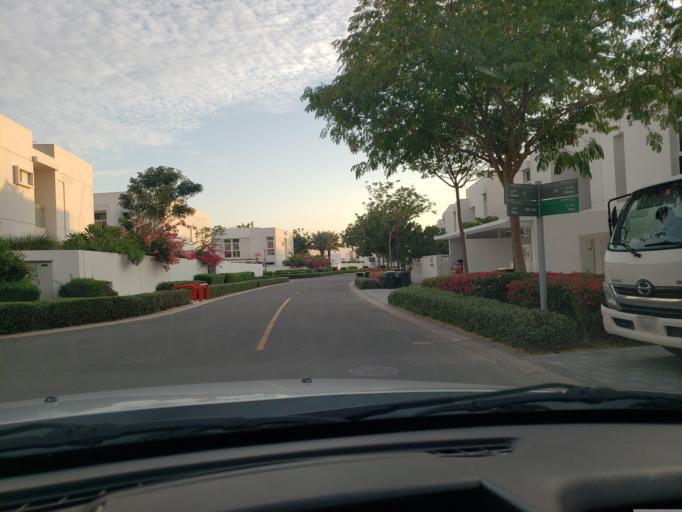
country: AE
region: Dubai
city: Dubai
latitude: 25.0172
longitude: 55.2718
